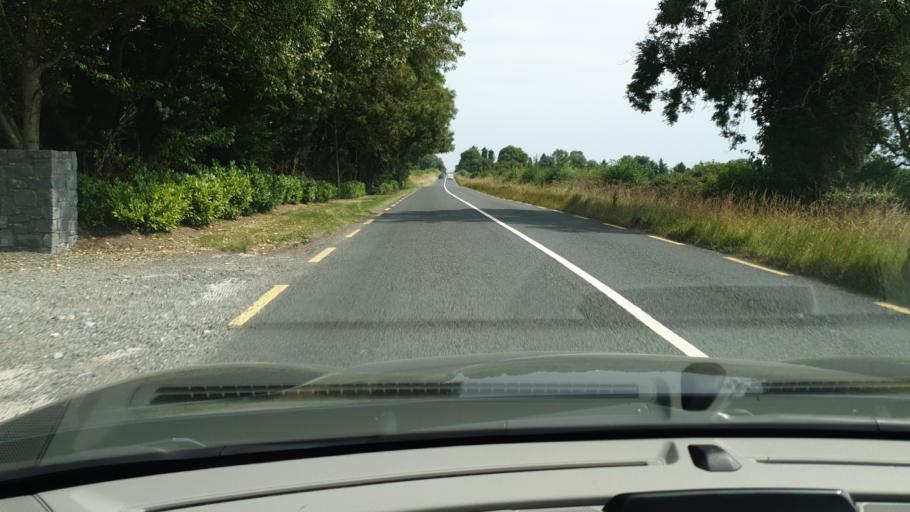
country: IE
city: Kentstown
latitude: 53.6344
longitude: -6.5830
